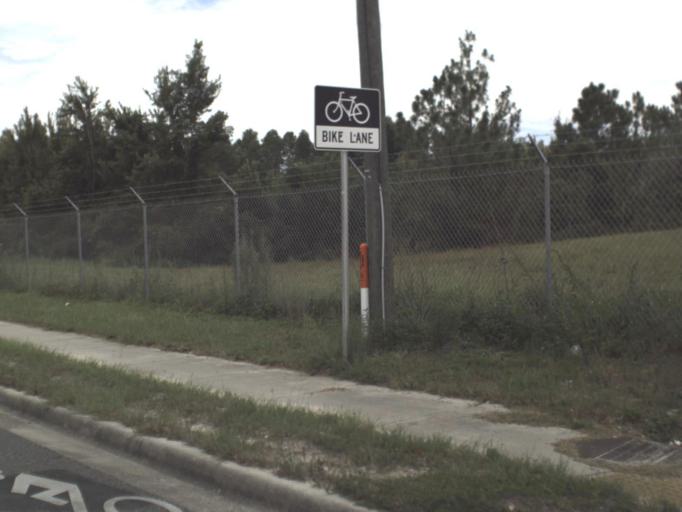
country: US
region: Florida
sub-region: Citrus County
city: Crystal River
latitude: 28.8953
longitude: -82.5574
